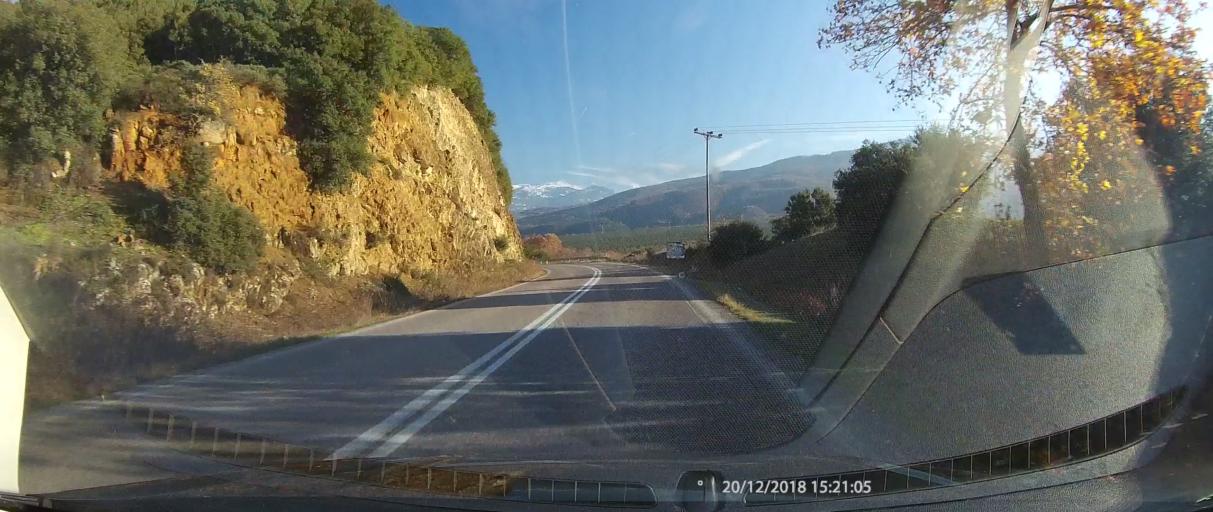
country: GR
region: Central Greece
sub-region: Nomos Fthiotidos
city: Makrakomi
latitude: 38.9311
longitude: 22.0678
